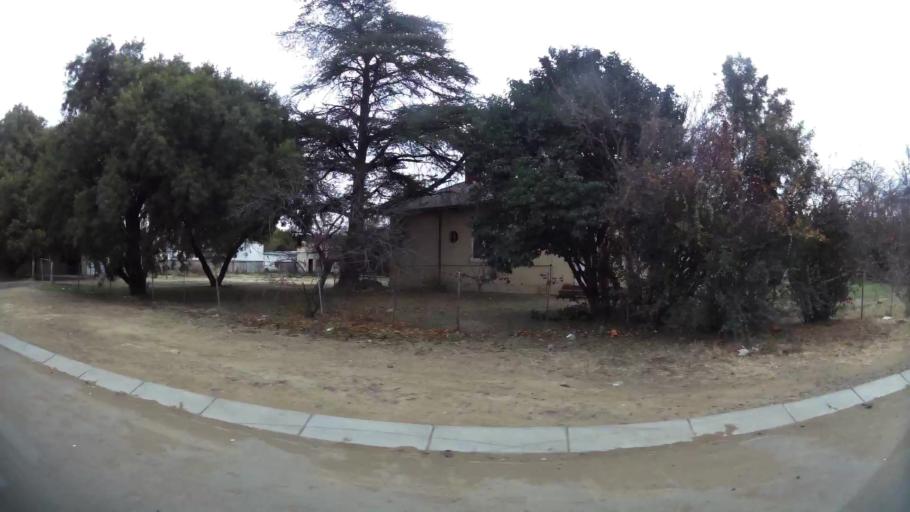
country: ZA
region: Orange Free State
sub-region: Fezile Dabi District Municipality
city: Kroonstad
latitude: -27.6603
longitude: 27.2474
